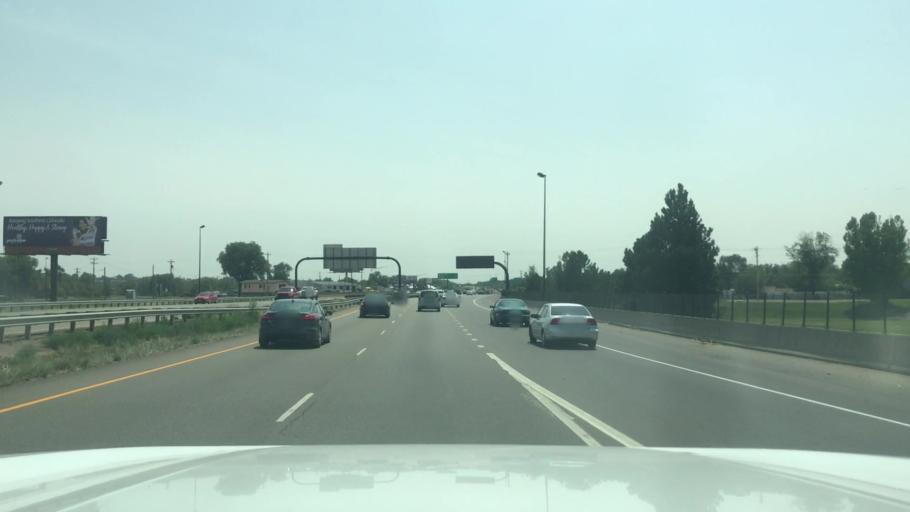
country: US
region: Colorado
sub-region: Pueblo County
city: Pueblo
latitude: 38.2955
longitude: -104.6104
